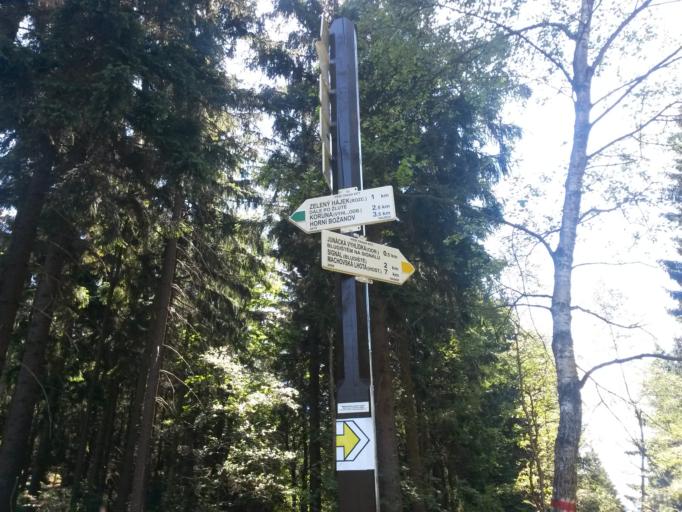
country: CZ
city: Machov
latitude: 50.5179
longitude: 16.3107
